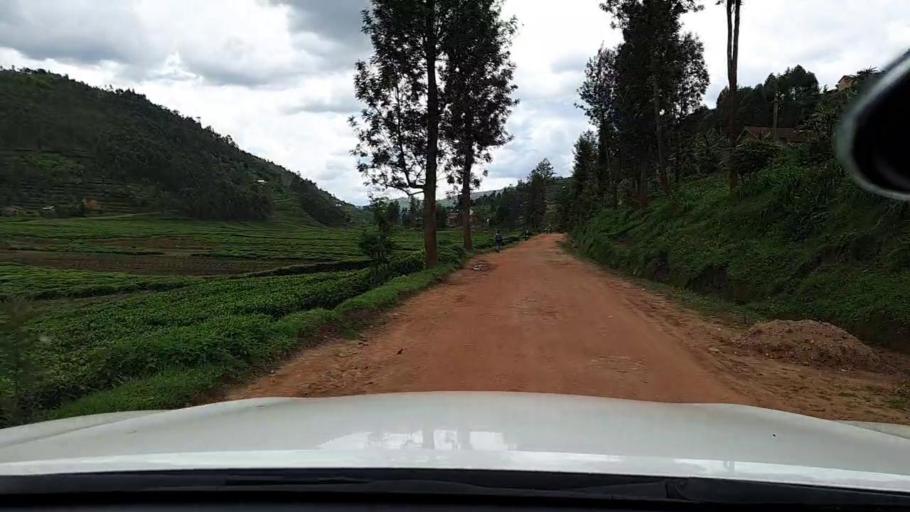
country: RW
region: Northern Province
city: Byumba
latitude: -1.6554
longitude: 29.9081
